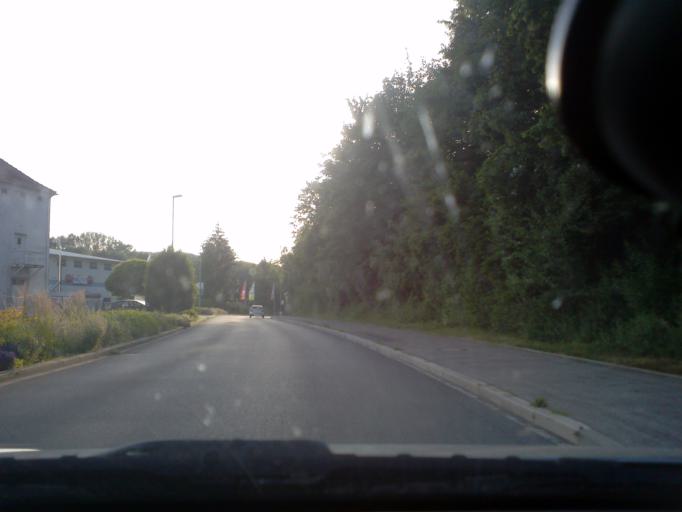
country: DE
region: Baden-Wuerttemberg
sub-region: Karlsruhe Region
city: Woessingen
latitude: 49.0154
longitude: 8.6020
